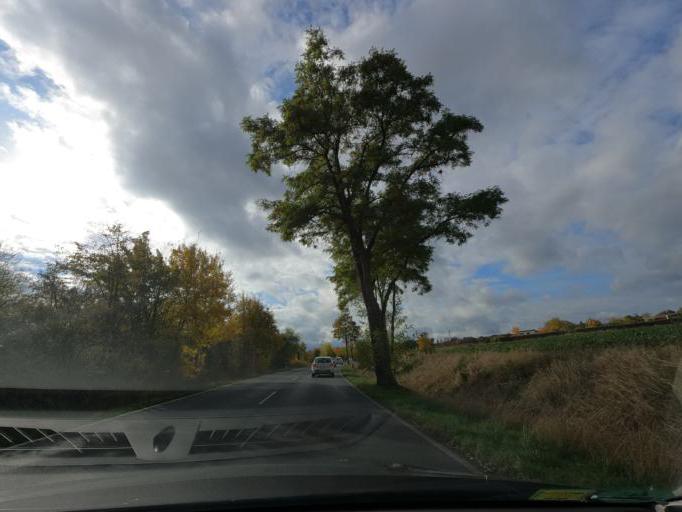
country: DE
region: Lower Saxony
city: Wolfenbuettel
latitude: 52.1426
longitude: 10.5371
